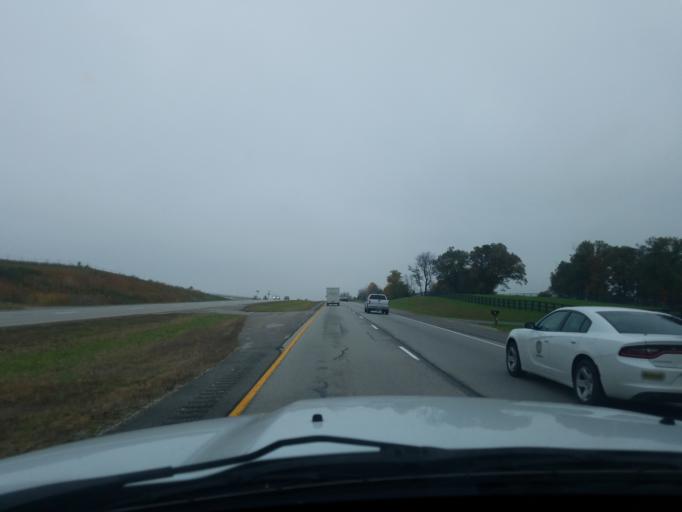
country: US
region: Kentucky
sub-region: Hardin County
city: Elizabethtown
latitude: 37.6527
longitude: -85.8368
